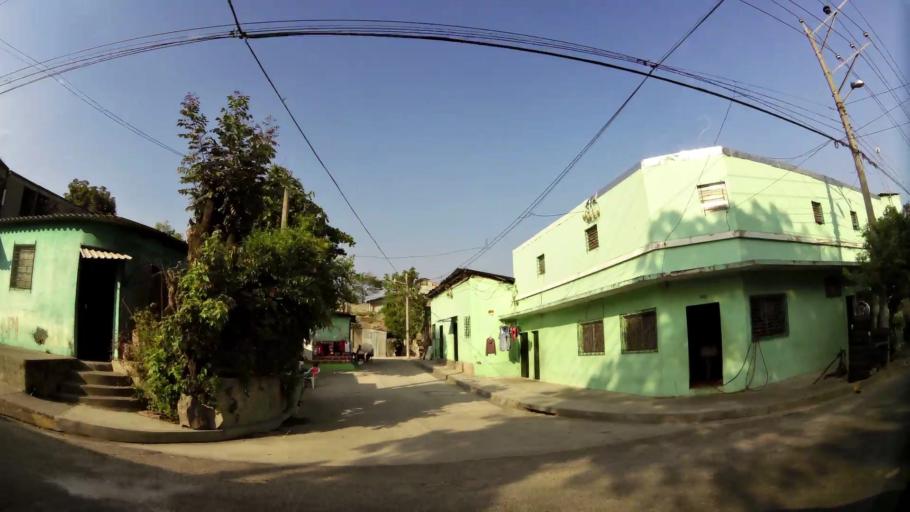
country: SV
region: San Salvador
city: San Salvador
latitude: 13.6973
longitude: -89.1788
